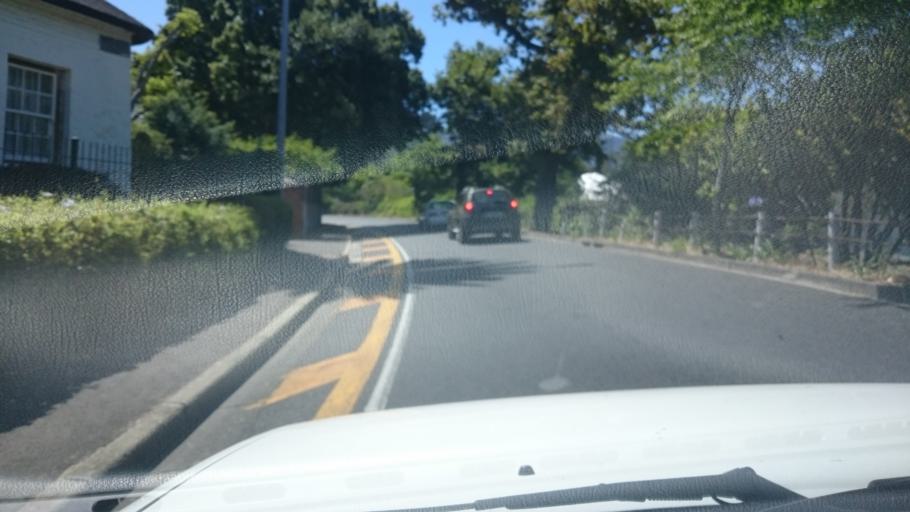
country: ZA
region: Western Cape
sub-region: City of Cape Town
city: Claremont
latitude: -34.0028
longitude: 18.4610
